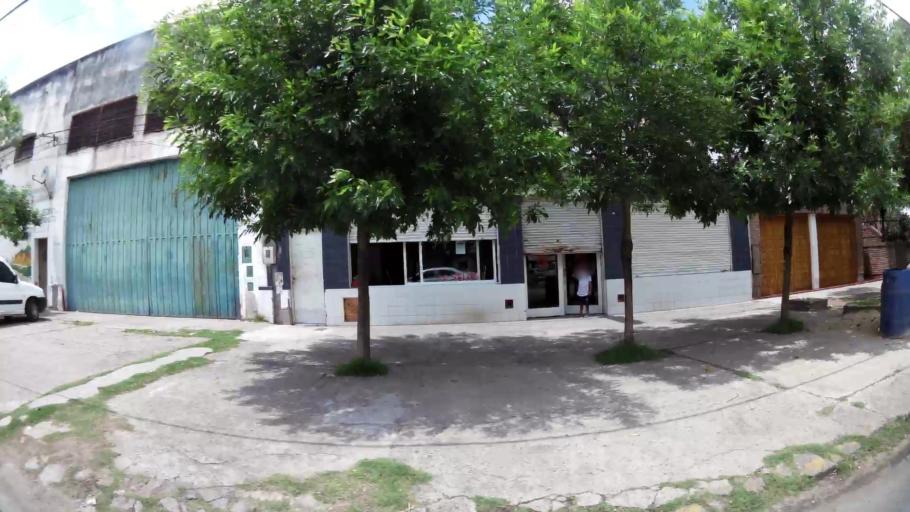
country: AR
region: Santa Fe
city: Gobernador Galvez
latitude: -32.9986
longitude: -60.6206
